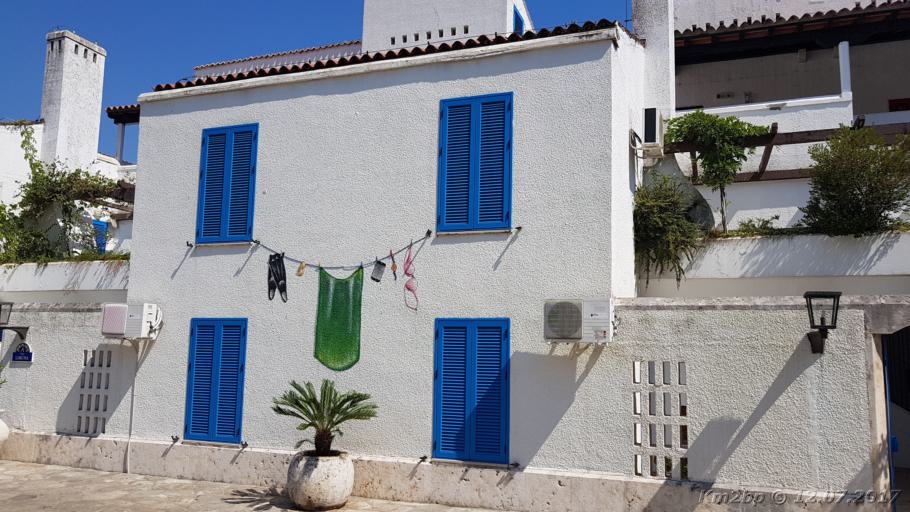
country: ME
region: Budva
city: Budva
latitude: 42.2869
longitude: 18.8475
